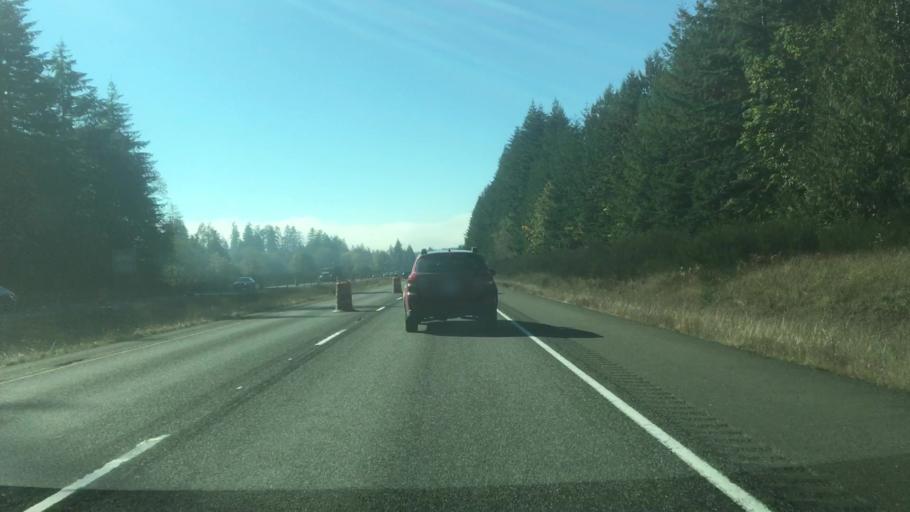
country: US
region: Washington
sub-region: Grays Harbor County
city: McCleary
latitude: 47.0521
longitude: -123.2955
